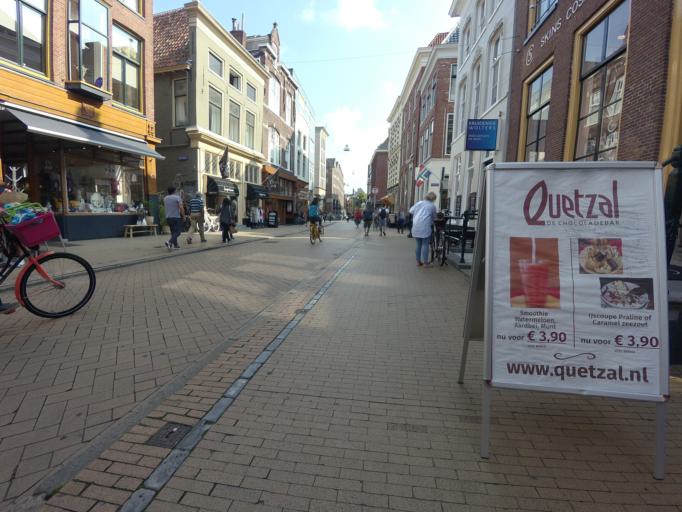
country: NL
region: Groningen
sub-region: Gemeente Groningen
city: Groningen
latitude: 53.2190
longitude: 6.5648
